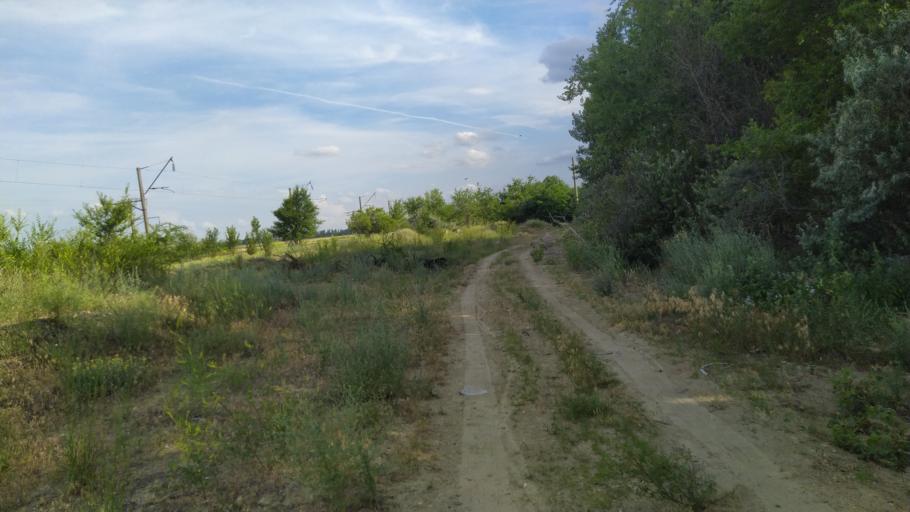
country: RU
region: Rostov
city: Bataysk
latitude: 47.1194
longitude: 39.7130
